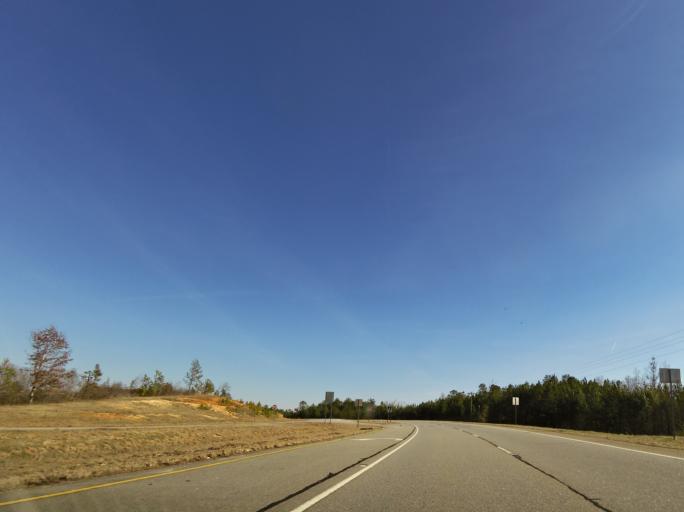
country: US
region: Georgia
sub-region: Upson County
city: Thomaston
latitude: 32.7453
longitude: -84.2345
